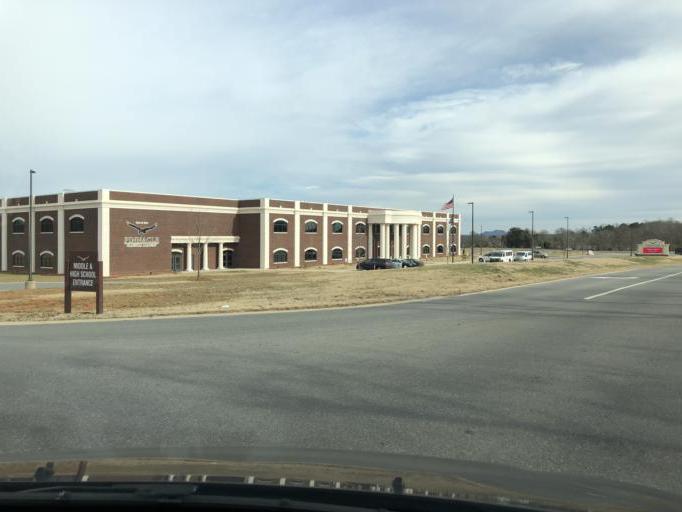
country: US
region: North Carolina
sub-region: Cleveland County
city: Shelby
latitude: 35.2533
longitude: -81.4980
